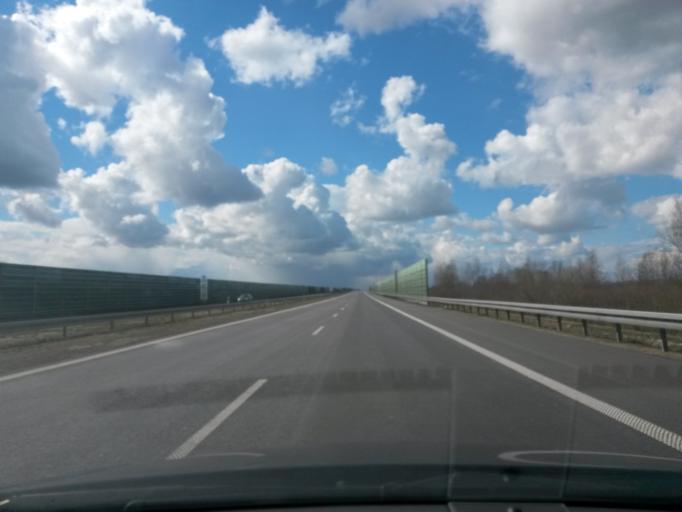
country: PL
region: Greater Poland Voivodeship
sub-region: Powiat kolski
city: Grzegorzew
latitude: 52.1202
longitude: 18.7033
